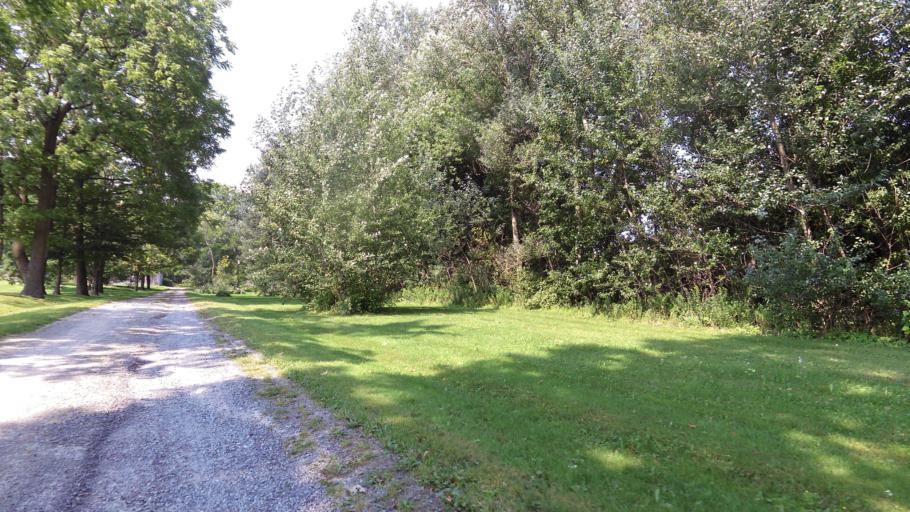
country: CA
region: Ontario
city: Prescott
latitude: 44.6554
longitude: -75.5869
